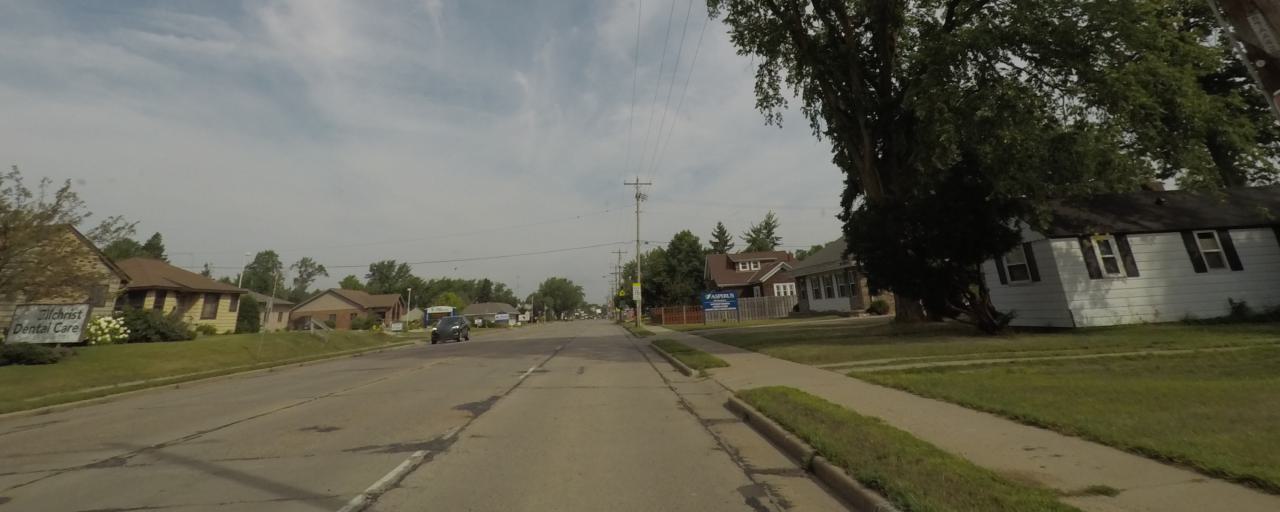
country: US
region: Wisconsin
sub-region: Portage County
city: Whiting
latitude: 44.5071
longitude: -89.5686
